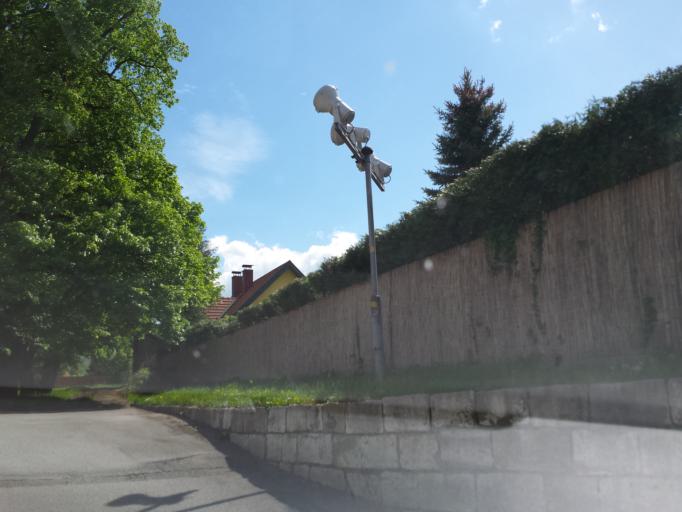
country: AT
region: Lower Austria
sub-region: Politischer Bezirk Wiener Neustadt
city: Markt Piesting
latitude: 47.8726
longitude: 16.1314
